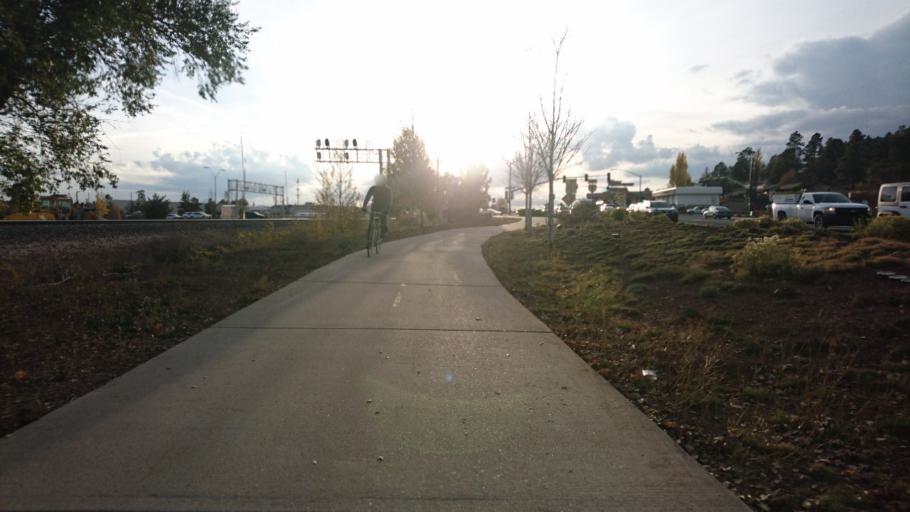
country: US
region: Arizona
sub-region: Coconino County
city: Flagstaff
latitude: 35.1953
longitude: -111.6270
